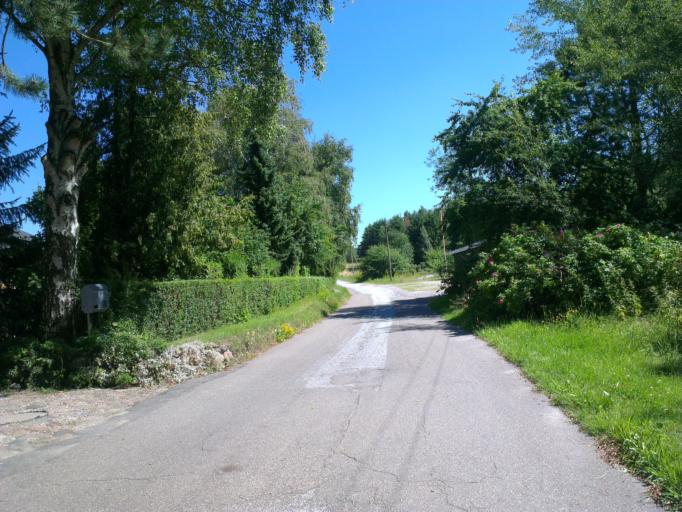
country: DK
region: Capital Region
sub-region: Frederikssund Kommune
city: Slangerup
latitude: 55.8291
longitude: 12.1836
